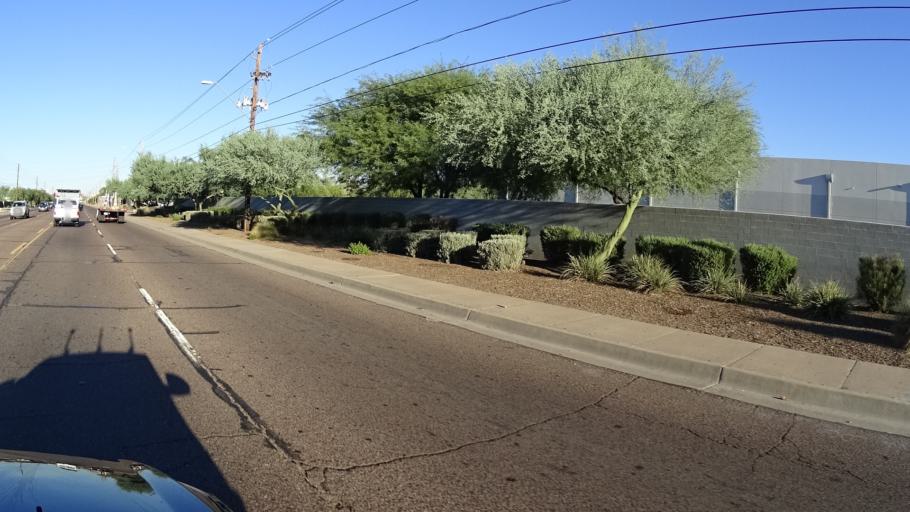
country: US
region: Arizona
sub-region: Maricopa County
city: Laveen
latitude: 33.4369
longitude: -112.1549
